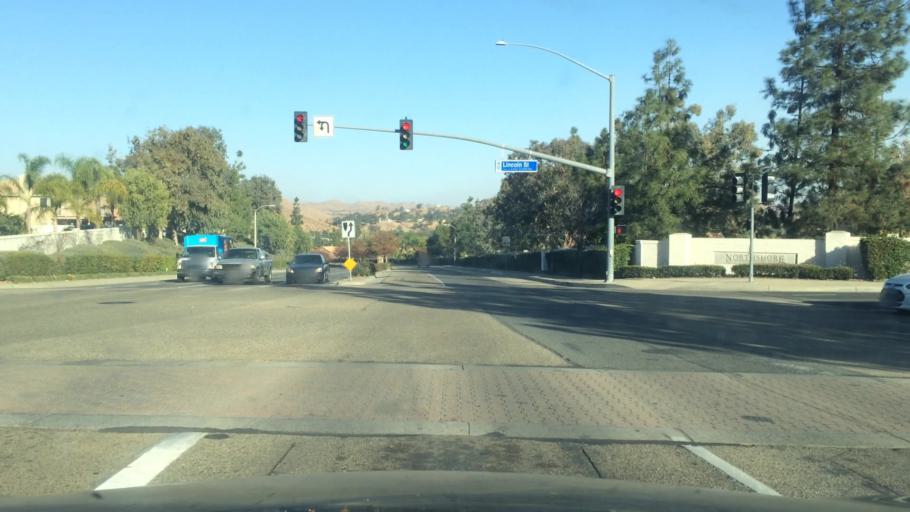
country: US
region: California
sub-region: Riverside County
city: Lake Elsinore
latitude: 33.6875
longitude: -117.3939
